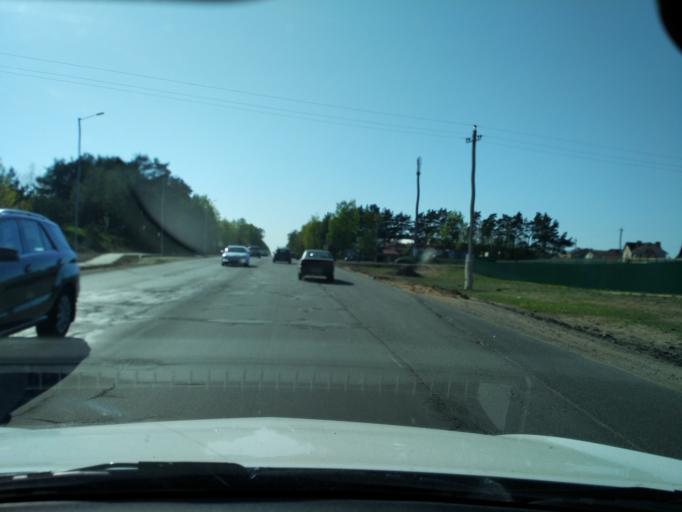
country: BY
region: Minsk
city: Borovlyany
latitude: 53.9650
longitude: 27.6670
